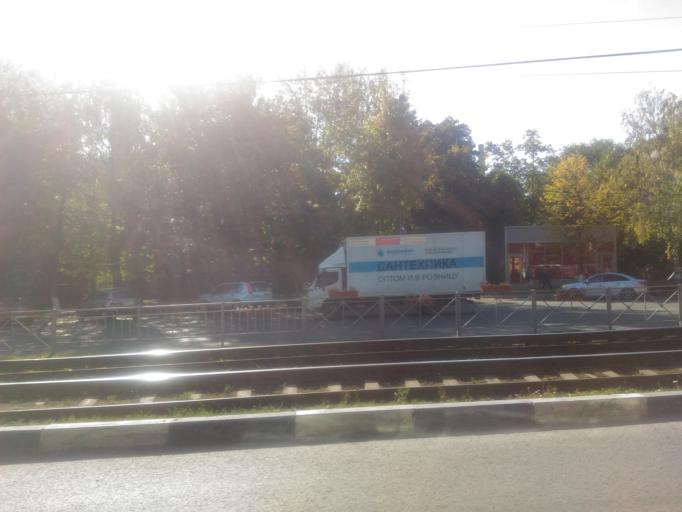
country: RU
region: Ulyanovsk
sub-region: Ulyanovskiy Rayon
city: Ulyanovsk
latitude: 54.3429
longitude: 48.3767
